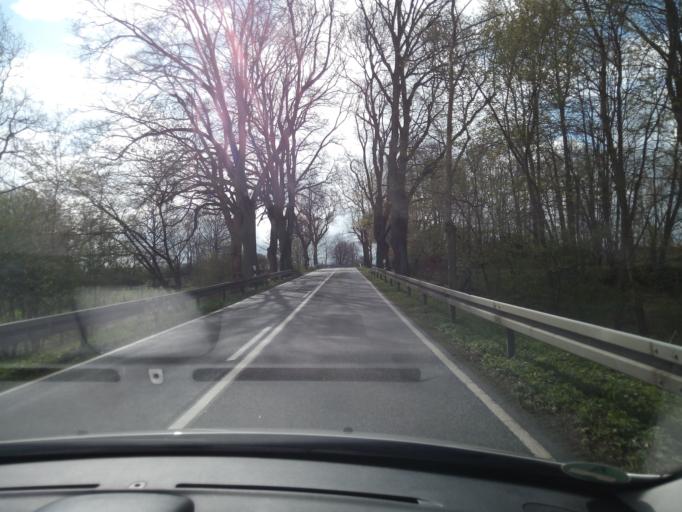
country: DE
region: Mecklenburg-Vorpommern
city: Loitz
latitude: 53.4110
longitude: 13.3636
